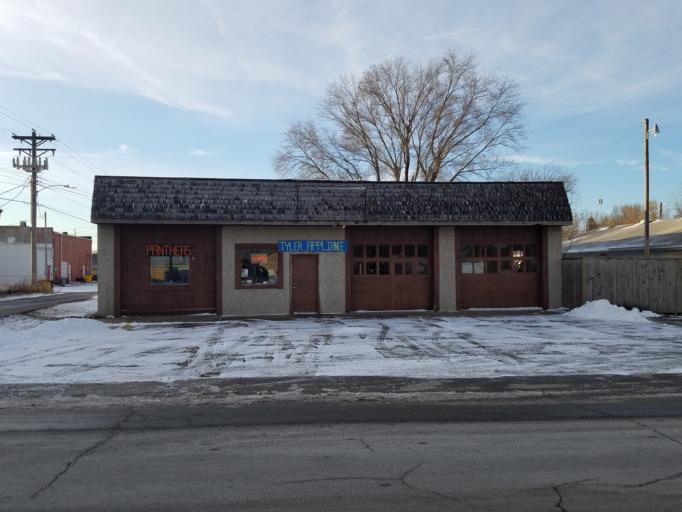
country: US
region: Missouri
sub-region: Jackson County
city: Oak Grove
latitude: 39.0045
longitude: -94.1298
